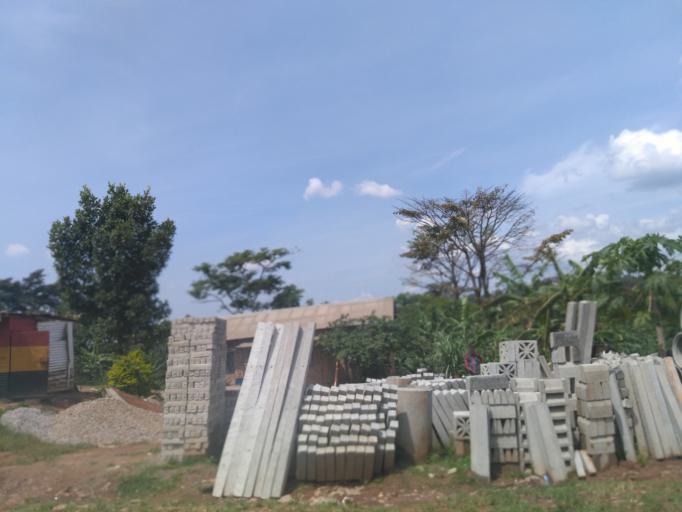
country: UG
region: Central Region
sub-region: Wakiso District
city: Bweyogerere
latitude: 0.4771
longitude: 32.6076
